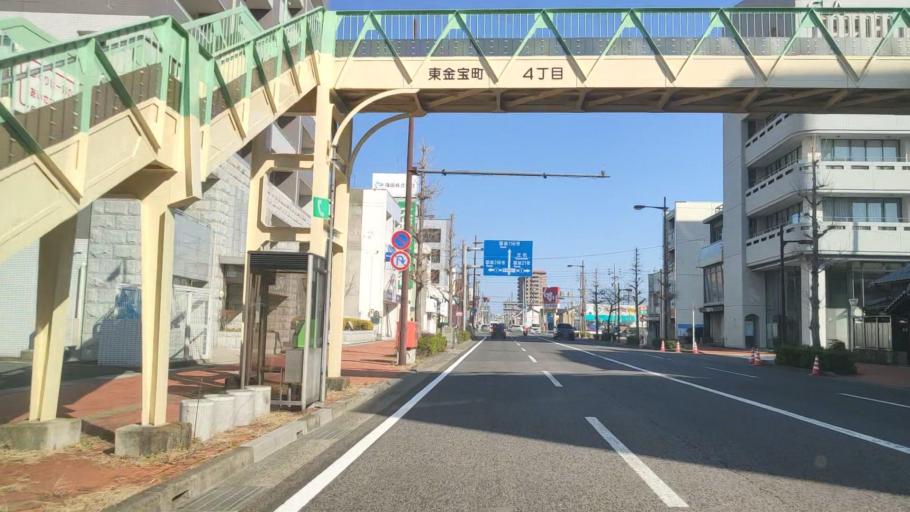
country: JP
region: Gifu
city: Gifu-shi
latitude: 35.4149
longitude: 136.7658
